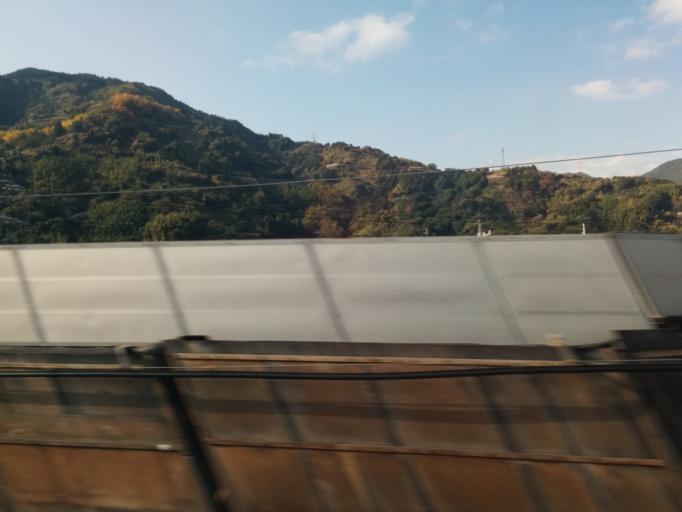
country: JP
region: Shizuoka
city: Shizuoka-shi
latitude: 35.0718
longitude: 138.5215
